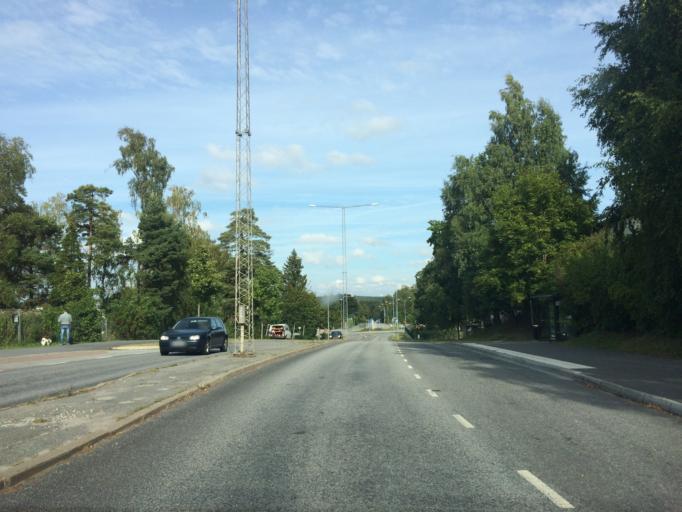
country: SE
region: Stockholm
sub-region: Sollentuna Kommun
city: Sollentuna
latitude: 59.4329
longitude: 17.9494
